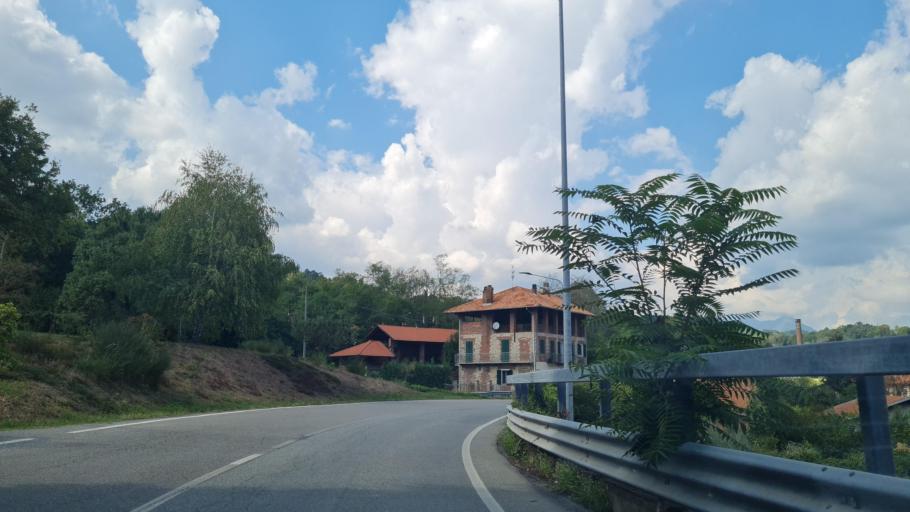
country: IT
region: Piedmont
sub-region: Provincia di Biella
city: Villa
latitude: 45.5956
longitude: 8.1829
